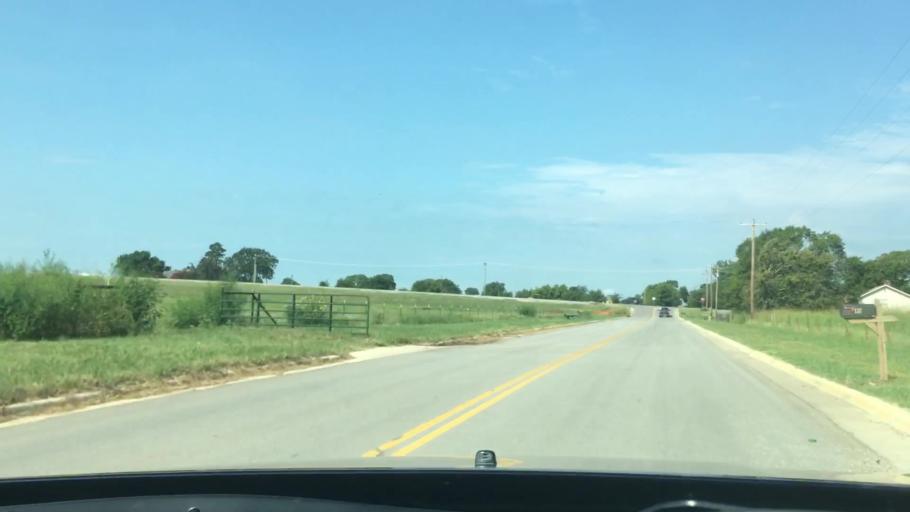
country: US
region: Oklahoma
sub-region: Bryan County
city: Durant
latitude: 33.9687
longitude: -96.3706
